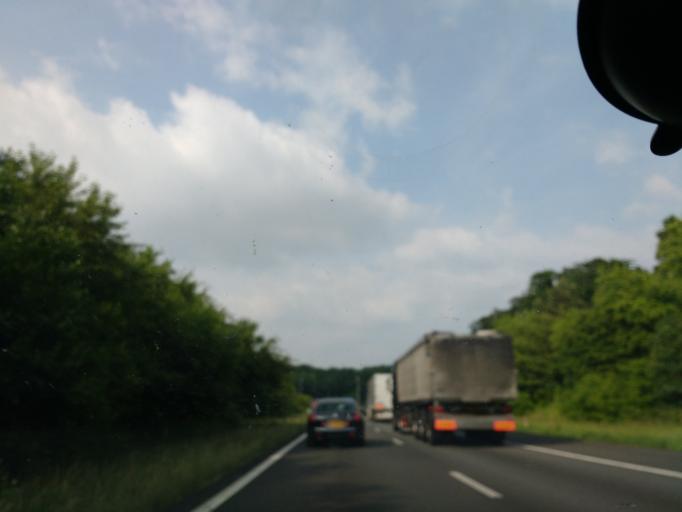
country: NL
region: Gelderland
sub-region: Gemeente Renkum
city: Wolfheze
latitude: 52.0245
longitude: 5.8226
